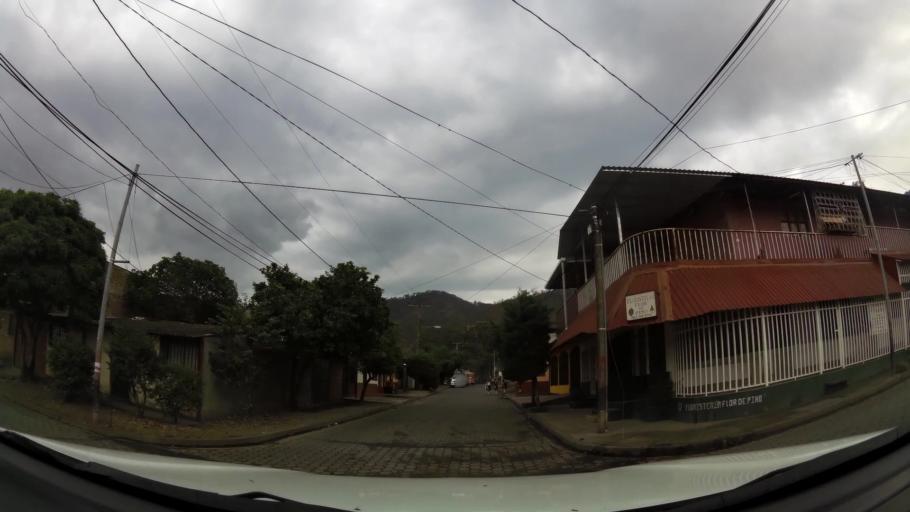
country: NI
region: Jinotega
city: Jinotega
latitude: 13.0850
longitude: -85.9968
